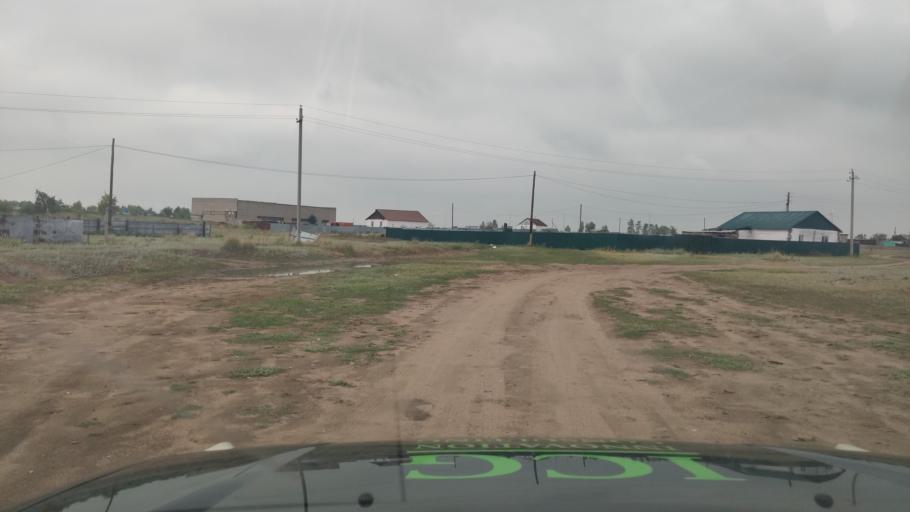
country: KZ
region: Pavlodar
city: Pavlodar
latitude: 52.1061
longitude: 77.0986
